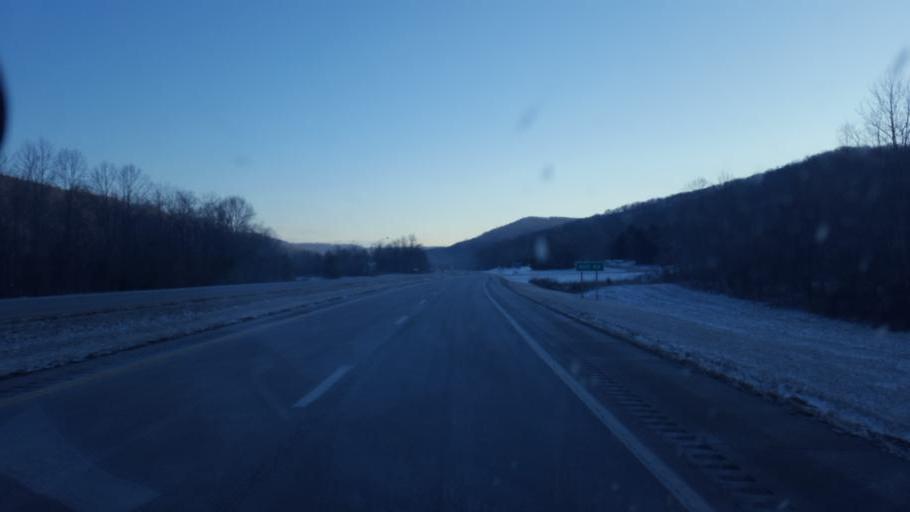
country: US
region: Ohio
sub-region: Adams County
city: Peebles
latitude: 39.0414
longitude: -83.2342
